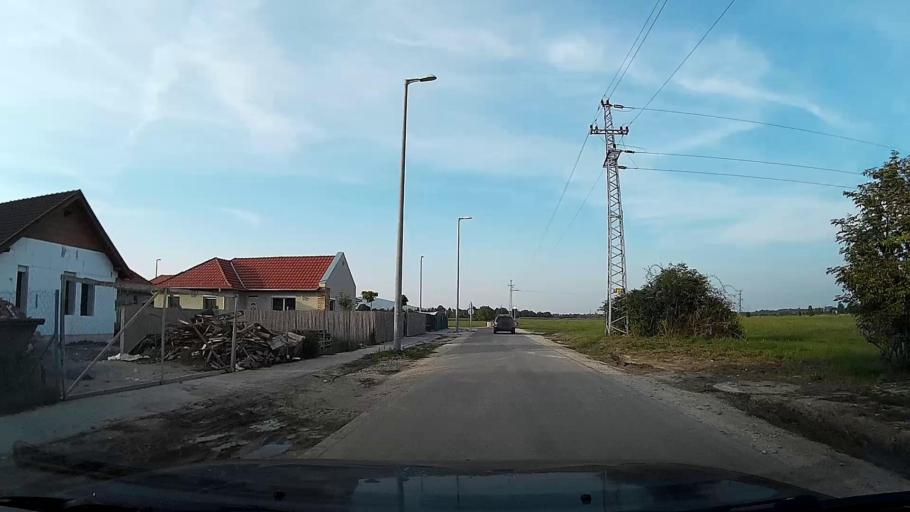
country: HU
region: Pest
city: Budakalasz
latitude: 47.6239
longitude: 19.0561
